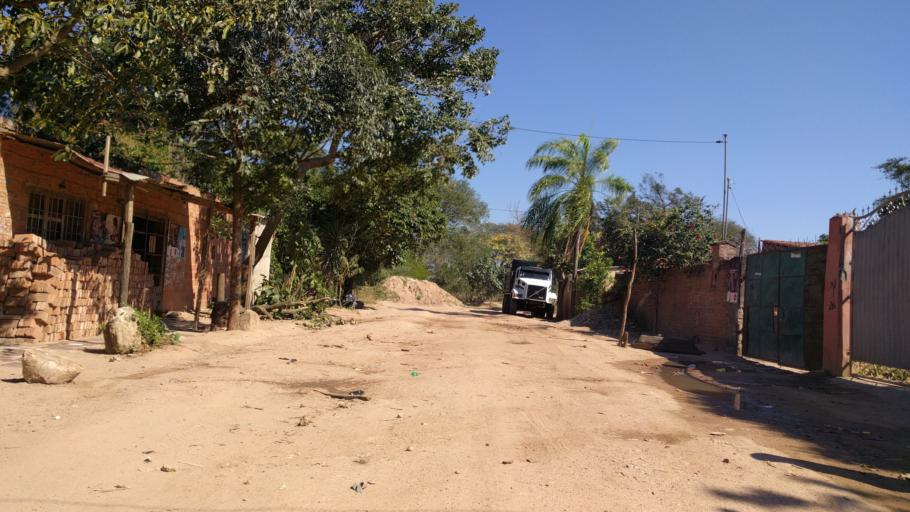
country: BO
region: Santa Cruz
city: Santa Cruz de la Sierra
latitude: -17.7889
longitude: -63.2269
